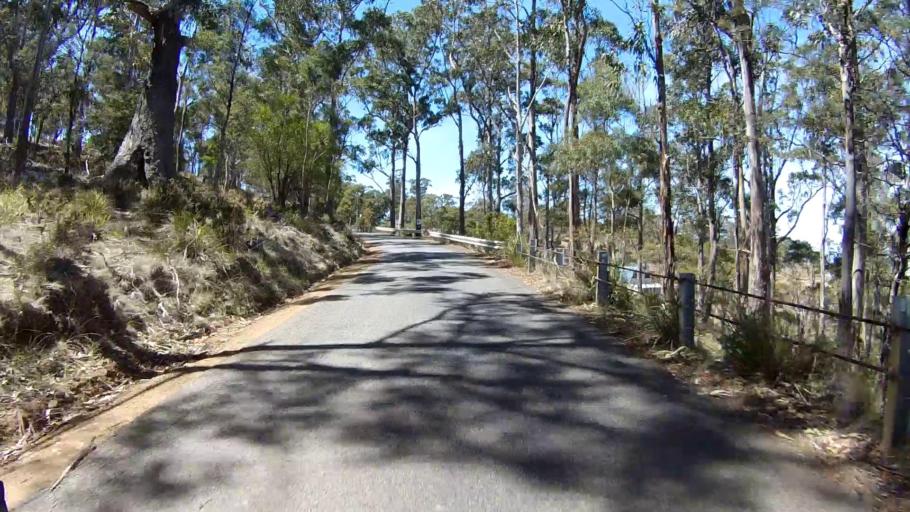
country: AU
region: Tasmania
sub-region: Clarence
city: Cambridge
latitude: -42.8576
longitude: 147.4430
